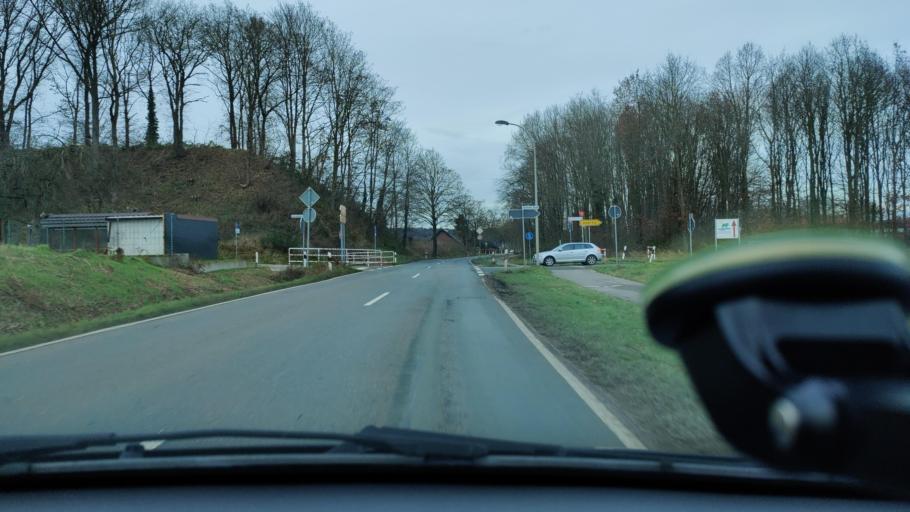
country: DE
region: North Rhine-Westphalia
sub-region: Regierungsbezirk Dusseldorf
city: Sonsbeck
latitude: 51.6551
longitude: 6.3700
